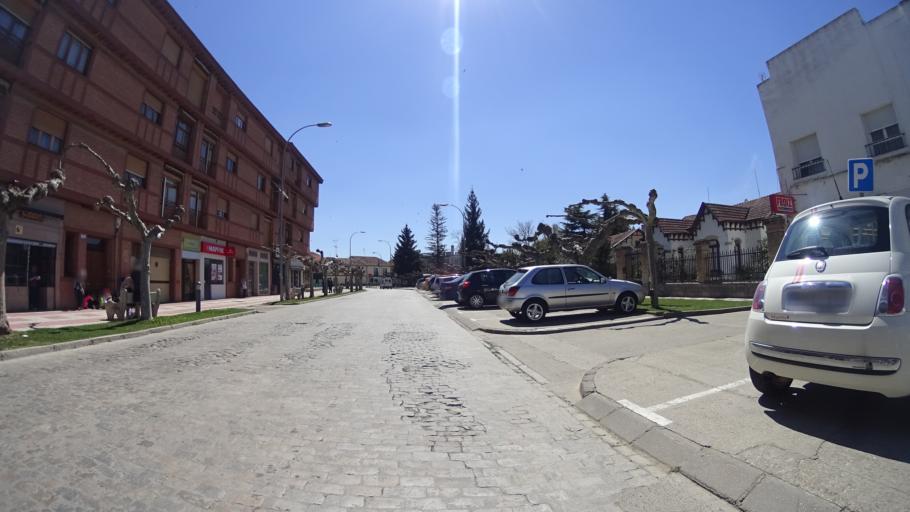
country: ES
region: Castille and Leon
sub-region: Provincia de Palencia
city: Duenas
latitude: 41.8738
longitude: -4.5446
